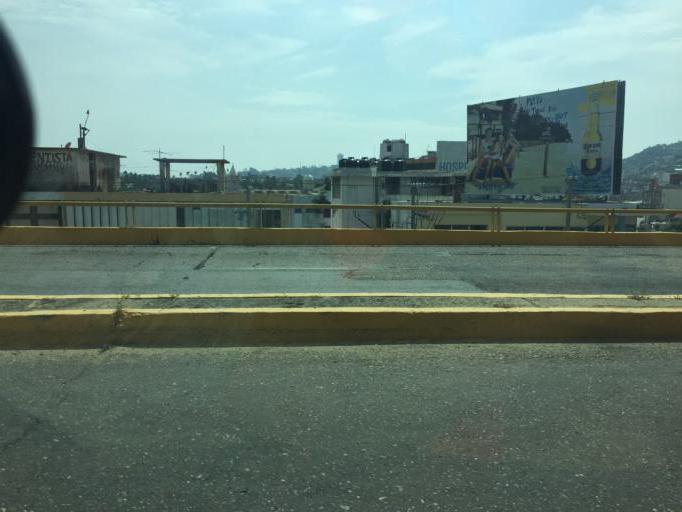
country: MX
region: Guerrero
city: Acapulco de Juarez
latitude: 16.8569
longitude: -99.9002
